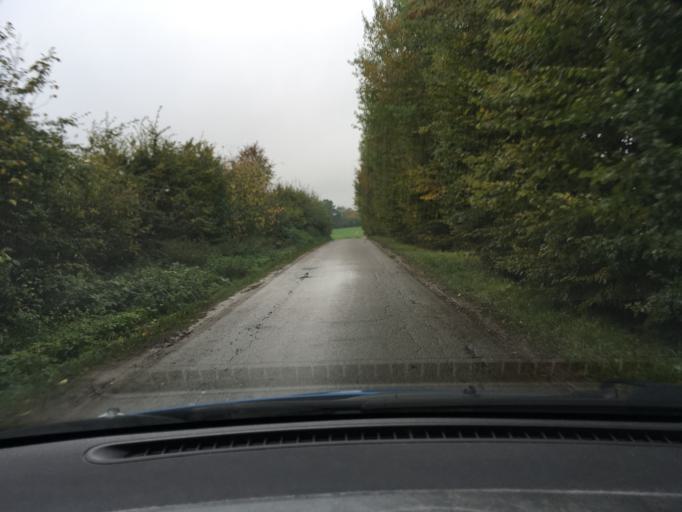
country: DE
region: Schleswig-Holstein
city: Bosau
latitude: 54.0984
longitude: 10.4654
